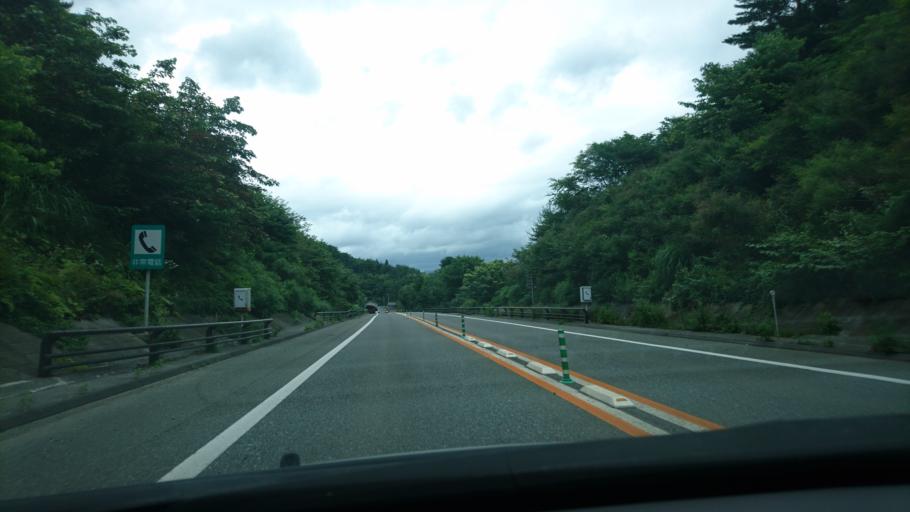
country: JP
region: Iwate
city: Ofunato
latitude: 39.0514
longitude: 141.7143
